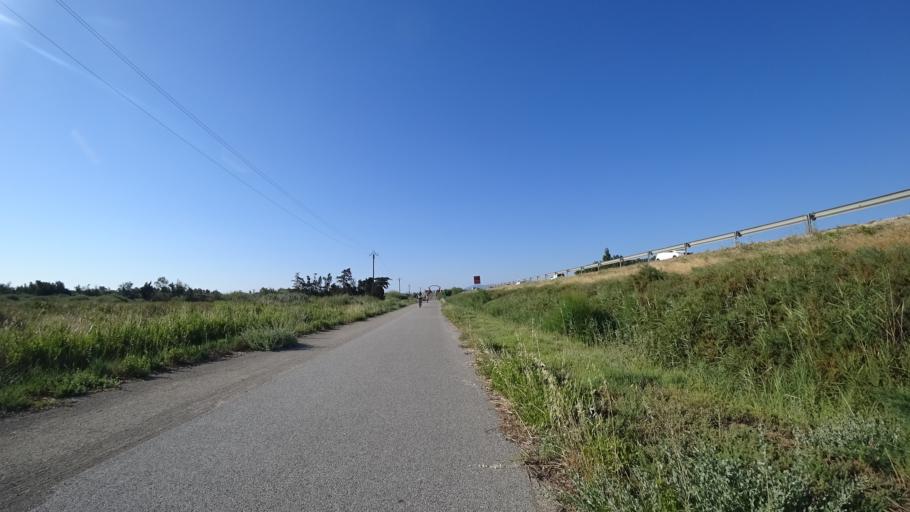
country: FR
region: Languedoc-Roussillon
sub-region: Departement des Pyrenees-Orientales
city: Sainte-Marie-Plage
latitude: 42.7420
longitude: 3.0240
